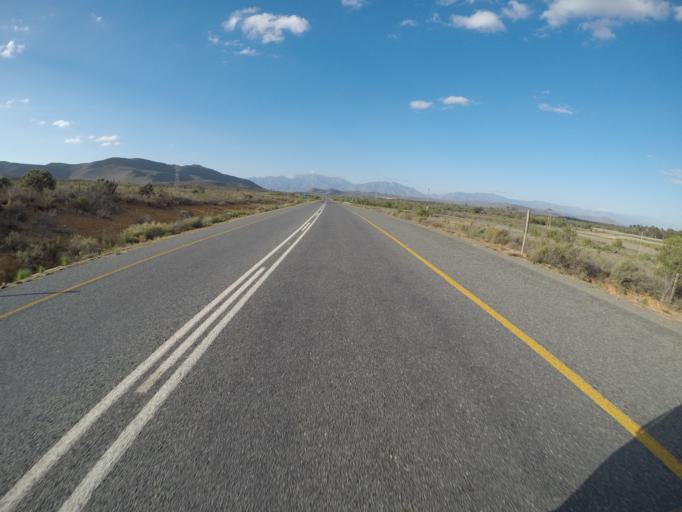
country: ZA
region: Western Cape
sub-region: Cape Winelands District Municipality
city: Worcester
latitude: -33.7760
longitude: 19.4691
